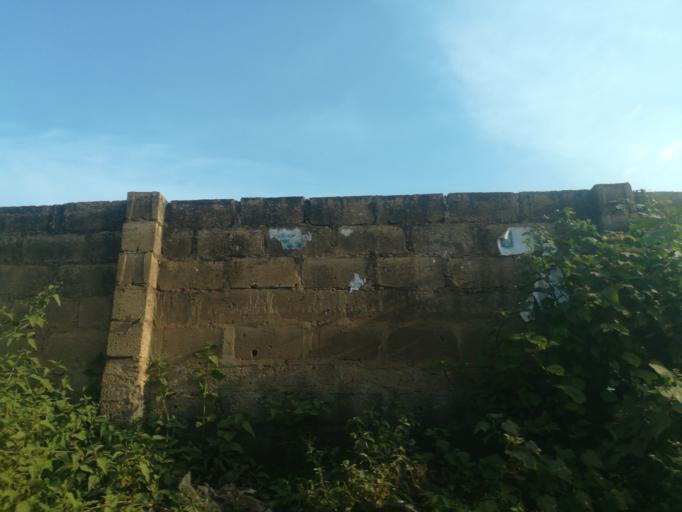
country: NG
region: Oyo
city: Moniya
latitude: 7.5523
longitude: 3.8901
